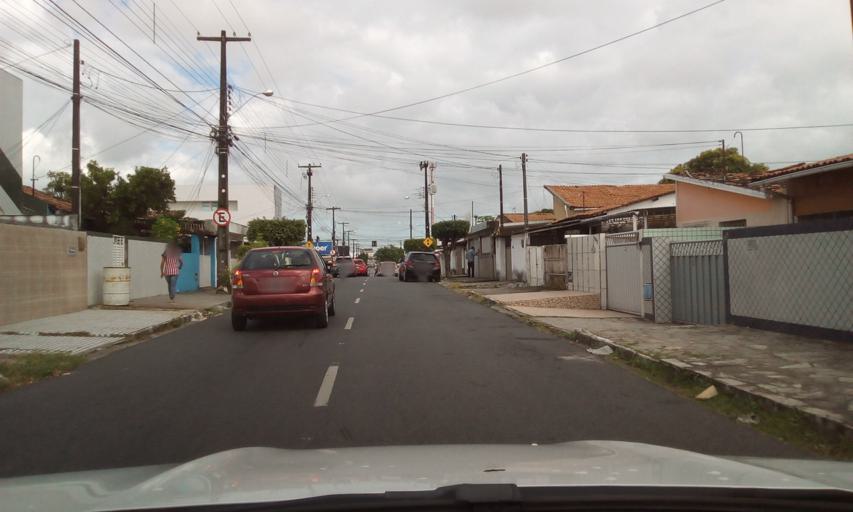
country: BR
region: Paraiba
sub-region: Joao Pessoa
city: Joao Pessoa
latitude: -7.1271
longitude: -34.8598
